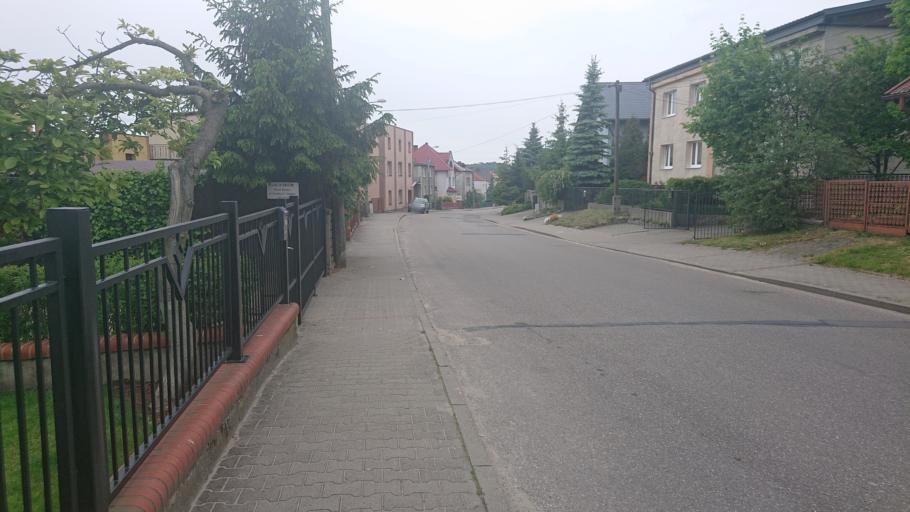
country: PL
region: Pomeranian Voivodeship
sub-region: Powiat chojnicki
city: Chojnice
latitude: 53.6972
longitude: 17.5663
